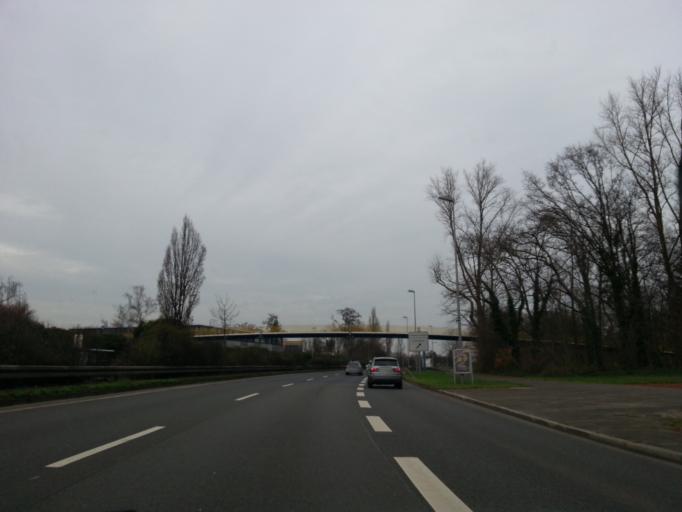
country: DE
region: North Rhine-Westphalia
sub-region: Regierungsbezirk Dusseldorf
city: Dusseldorf
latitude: 51.2578
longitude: 6.7625
